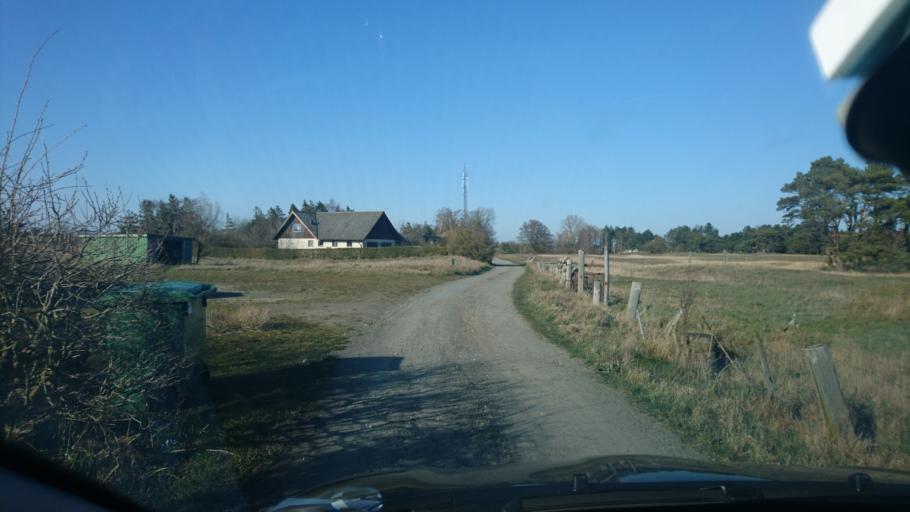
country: SE
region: Skane
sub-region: Simrishamns Kommun
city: Simrishamn
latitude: 55.4191
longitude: 14.2065
